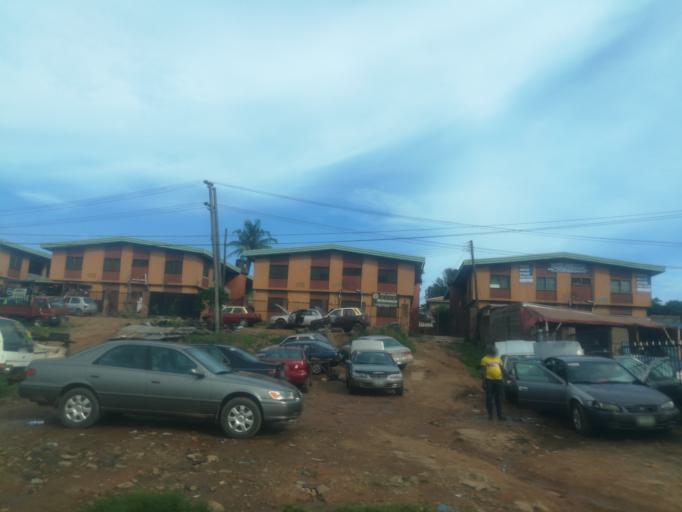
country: NG
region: Oyo
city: Ibadan
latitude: 7.3967
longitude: 3.9390
